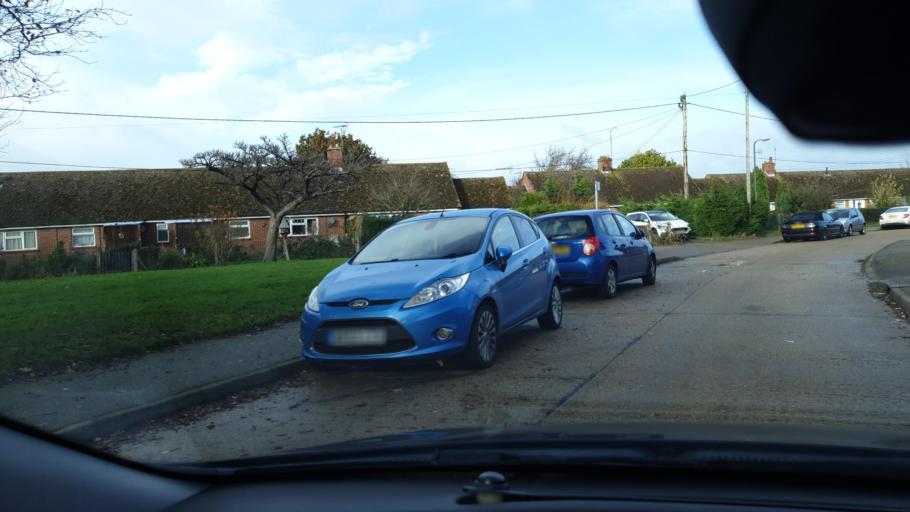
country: GB
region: England
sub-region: Essex
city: Dovercourt
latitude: 51.9236
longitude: 1.2283
